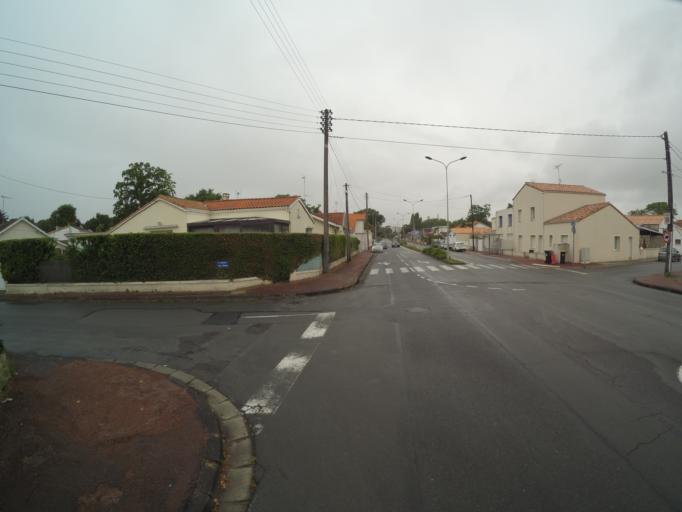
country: FR
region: Poitou-Charentes
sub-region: Departement de la Charente-Maritime
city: Saint-Georges-de-Didonne
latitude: 45.6158
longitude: -1.0021
